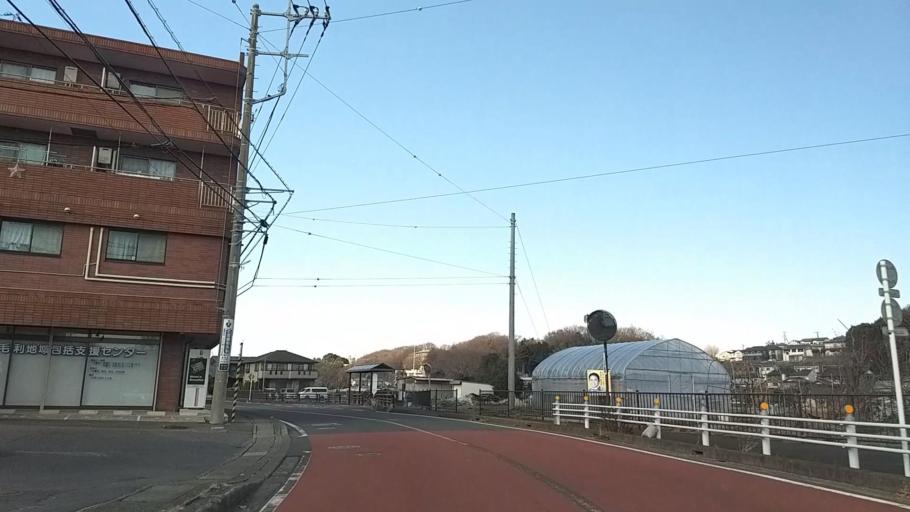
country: JP
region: Kanagawa
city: Atsugi
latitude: 35.4428
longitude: 139.3351
